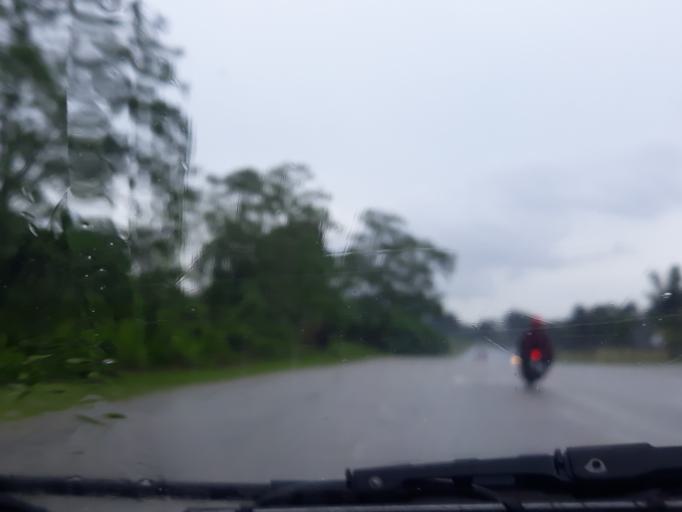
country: MY
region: Kedah
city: Kulim
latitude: 5.3505
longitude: 100.5850
